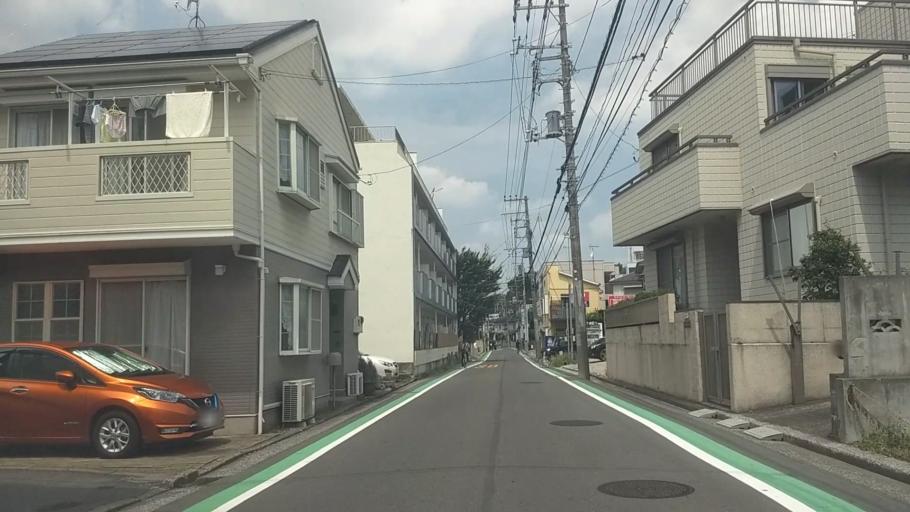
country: JP
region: Kanagawa
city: Yokohama
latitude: 35.5067
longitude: 139.6350
